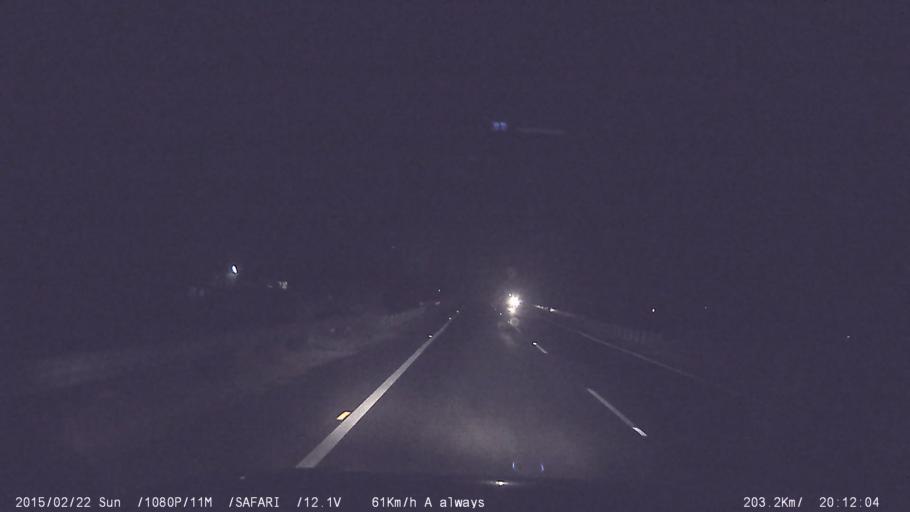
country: IN
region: Tamil Nadu
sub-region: Dindigul
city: Nilakottai
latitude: 10.2349
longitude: 77.8173
